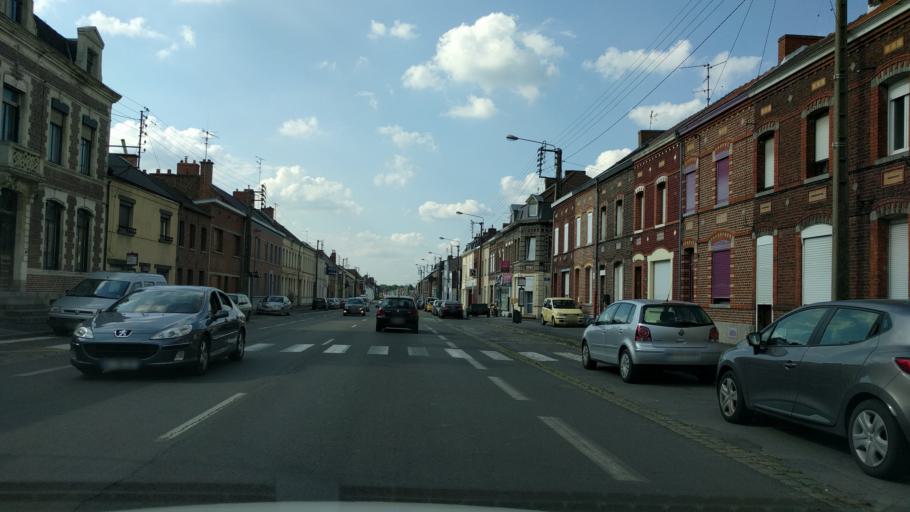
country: FR
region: Nord-Pas-de-Calais
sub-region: Departement du Nord
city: Beuvrages
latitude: 50.3844
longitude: 3.4909
